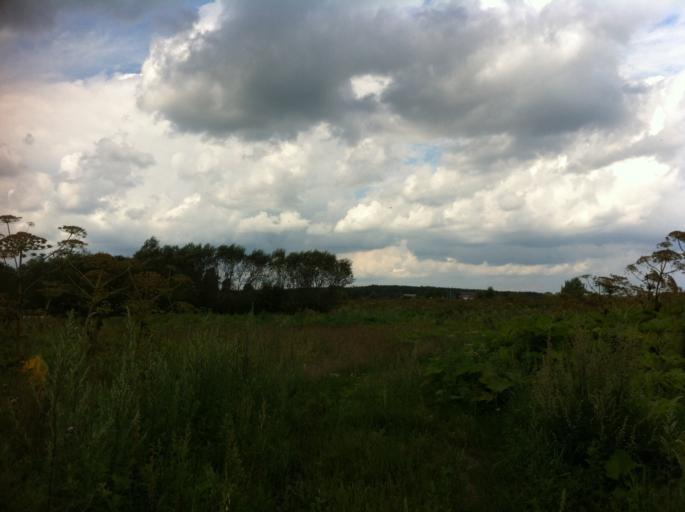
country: RU
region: Pskov
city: Izborsk
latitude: 57.8155
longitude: 27.9628
